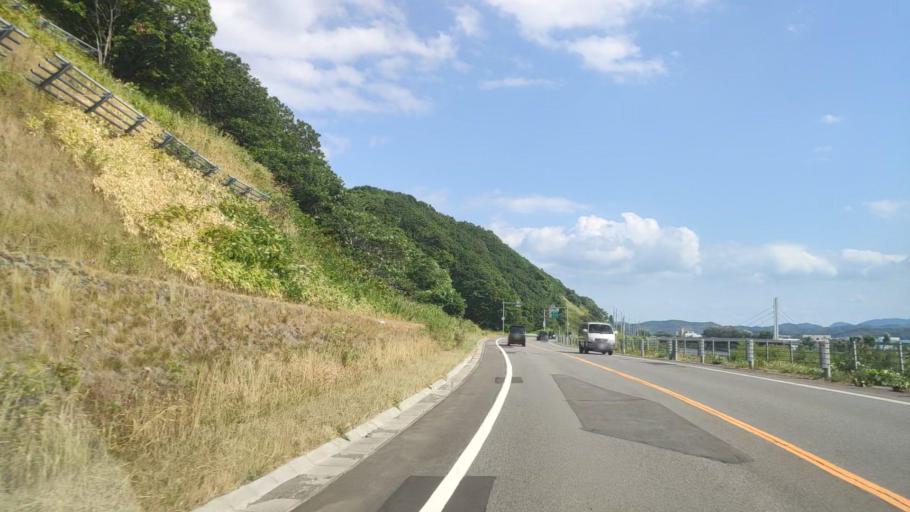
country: JP
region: Hokkaido
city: Rumoi
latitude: 43.9507
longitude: 141.6465
